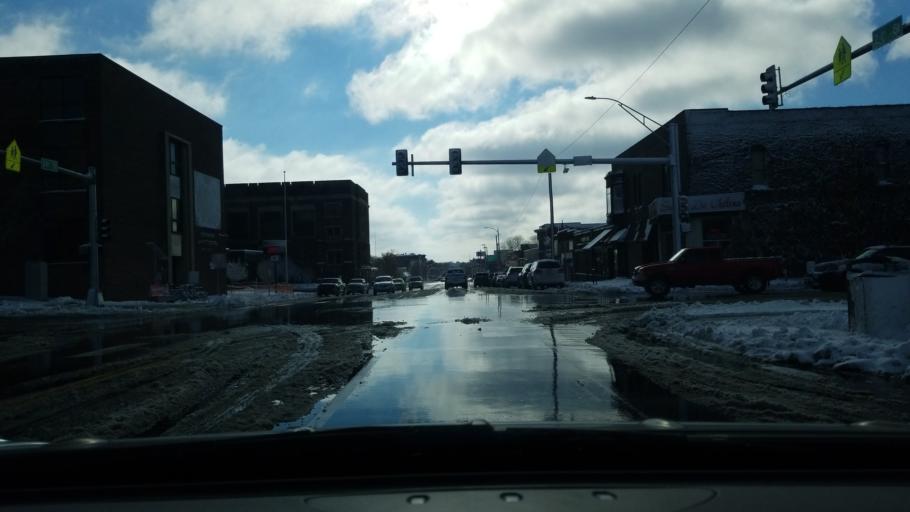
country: US
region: Nebraska
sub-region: Douglas County
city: Omaha
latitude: 41.2149
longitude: -95.9471
